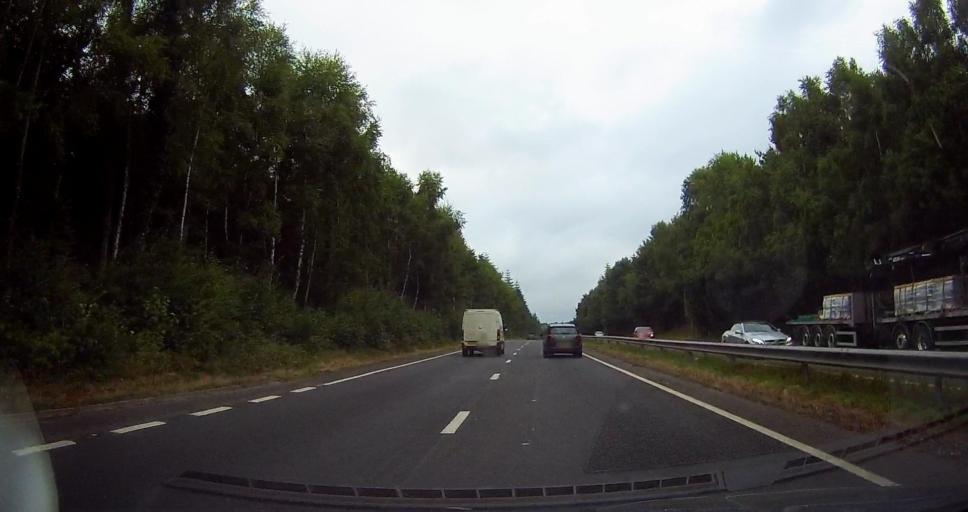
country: GB
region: England
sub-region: Devon
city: Kingsteignton
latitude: 50.5728
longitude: -3.5962
